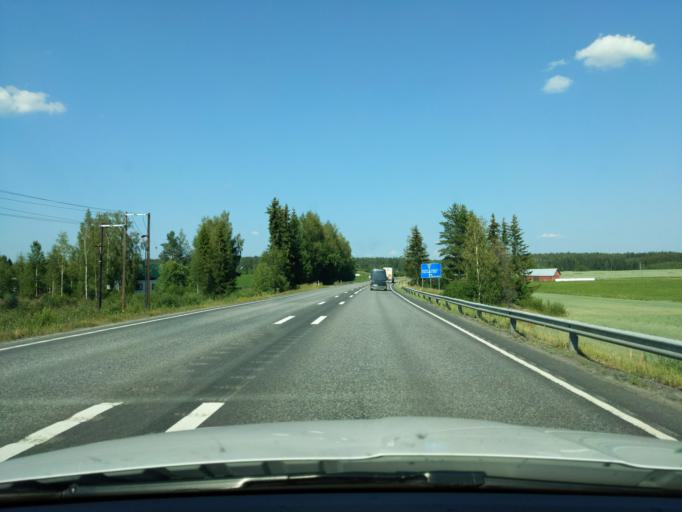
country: FI
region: Paijanne Tavastia
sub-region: Lahti
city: Hollola
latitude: 60.9465
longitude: 25.4156
